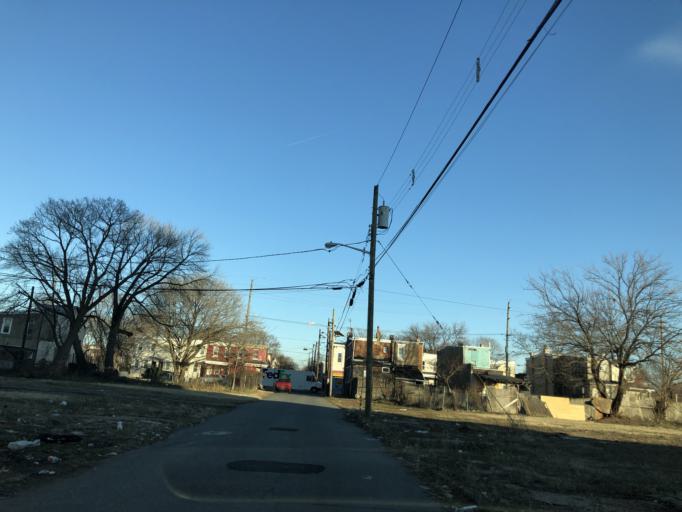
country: US
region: New Jersey
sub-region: Camden County
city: Camden
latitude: 39.9312
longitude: -75.1249
